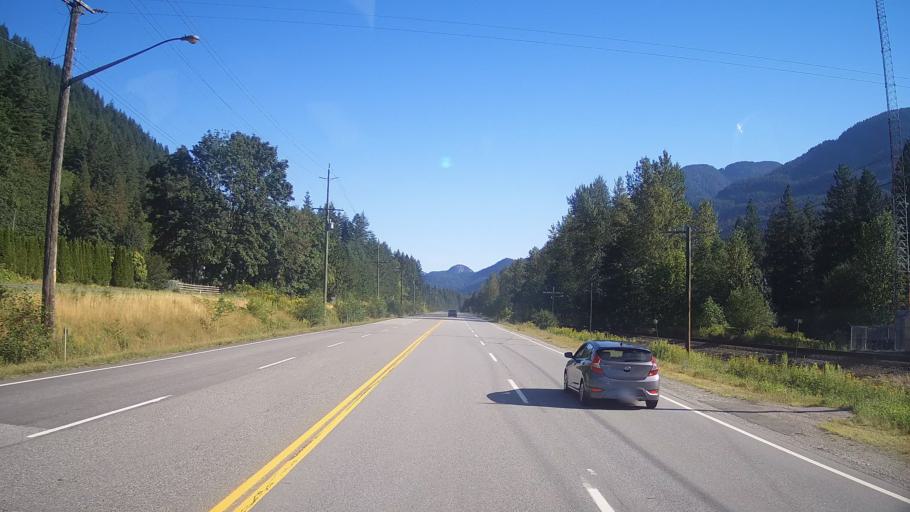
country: CA
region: British Columbia
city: Hope
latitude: 49.4916
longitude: -121.4208
